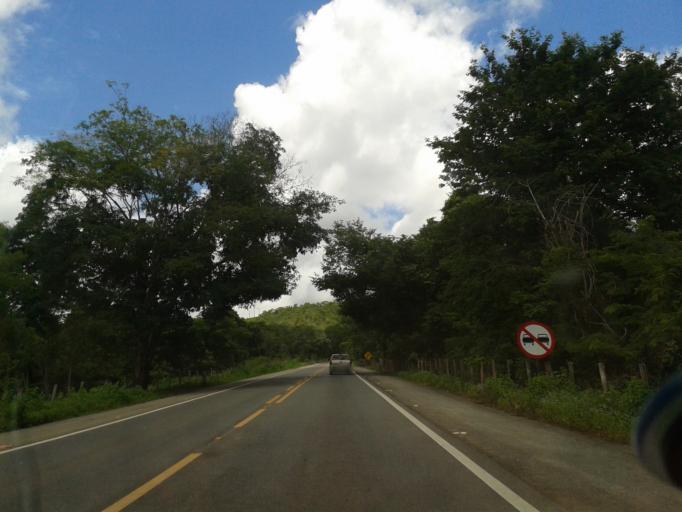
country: BR
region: Goias
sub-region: Goias
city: Goias
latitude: -15.8818
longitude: -50.1038
